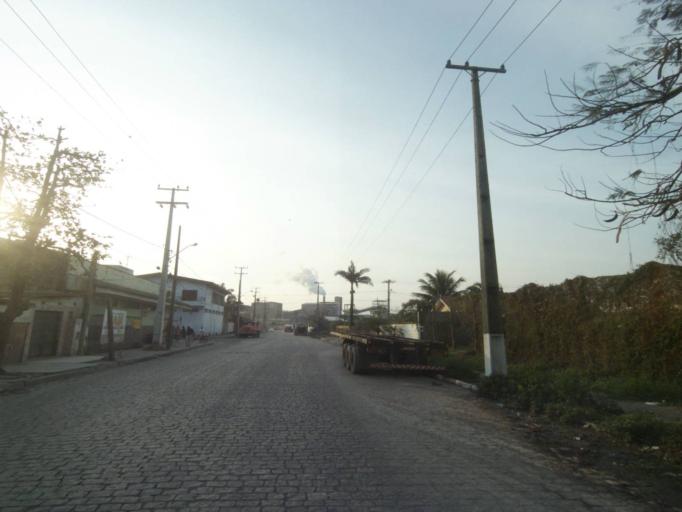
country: BR
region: Parana
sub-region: Paranagua
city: Paranagua
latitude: -25.5125
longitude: -48.5369
